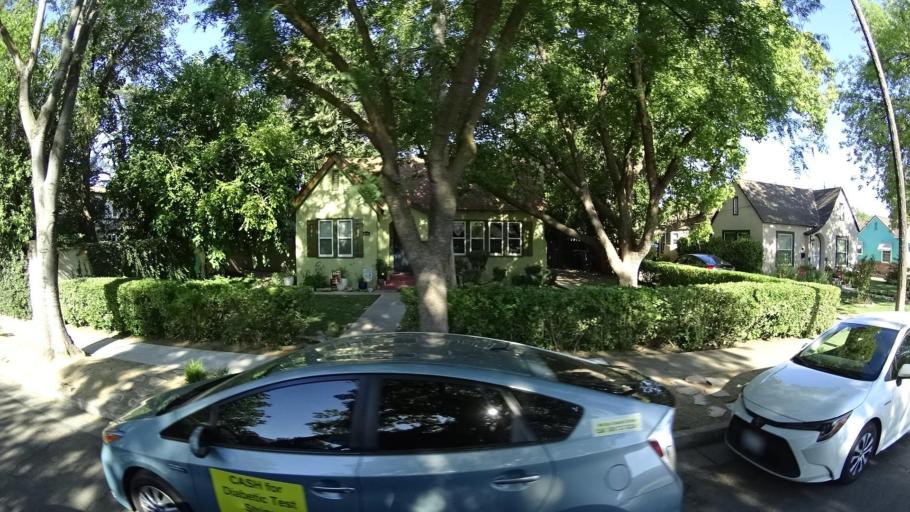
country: US
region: California
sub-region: Fresno County
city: Fresno
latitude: 36.7673
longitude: -119.8143
